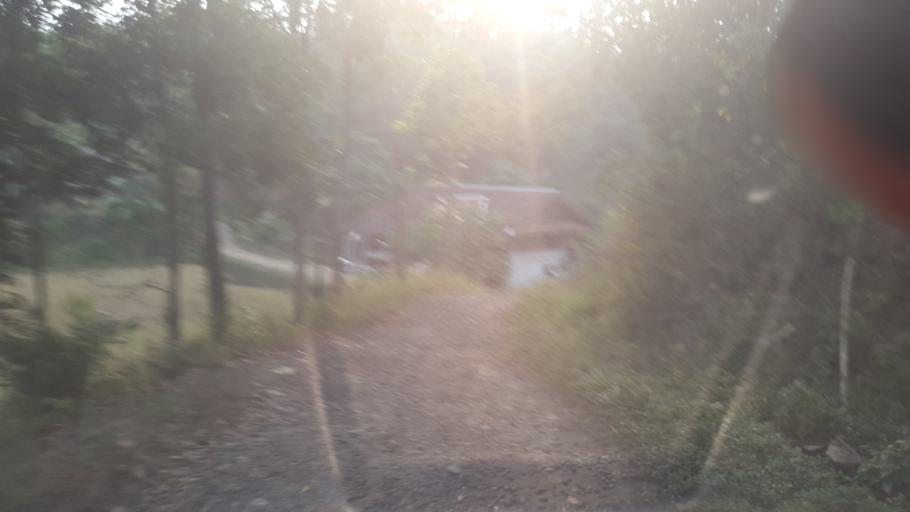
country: ID
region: West Java
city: Sukamaju
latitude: -6.9997
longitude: 106.8809
